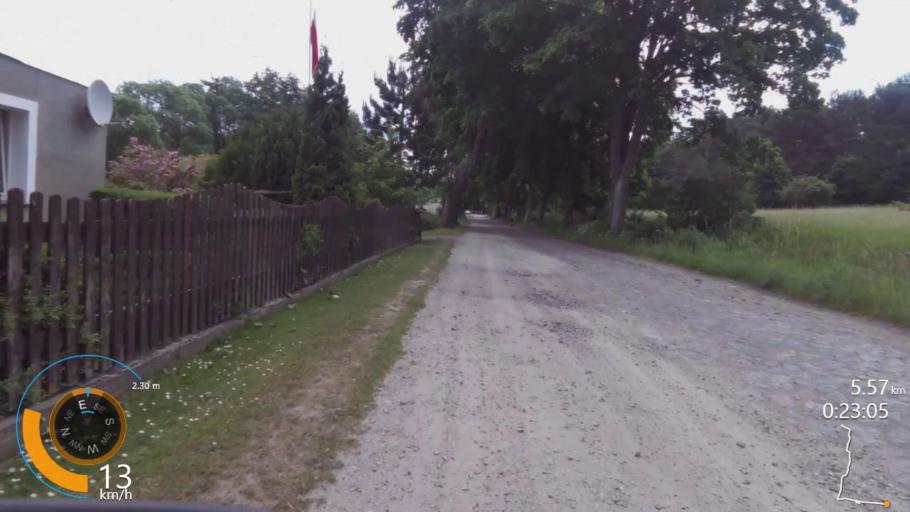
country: PL
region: West Pomeranian Voivodeship
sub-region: Powiat kamienski
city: Miedzyzdroje
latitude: 53.8782
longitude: 14.4530
